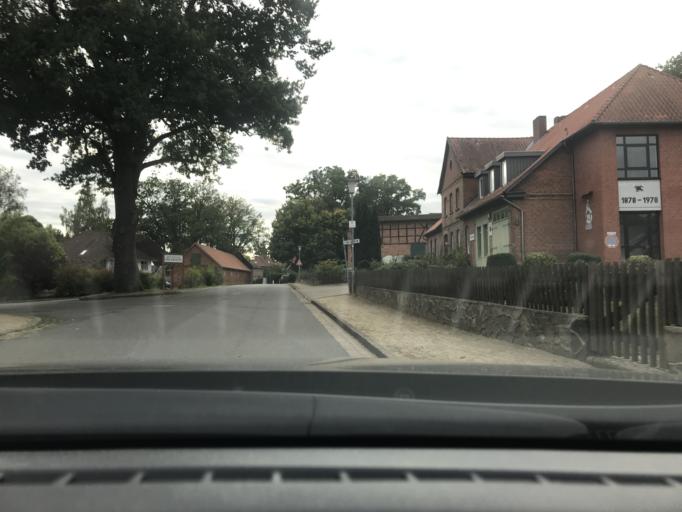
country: DE
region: Lower Saxony
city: Suderburg
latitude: 52.8978
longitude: 10.4533
